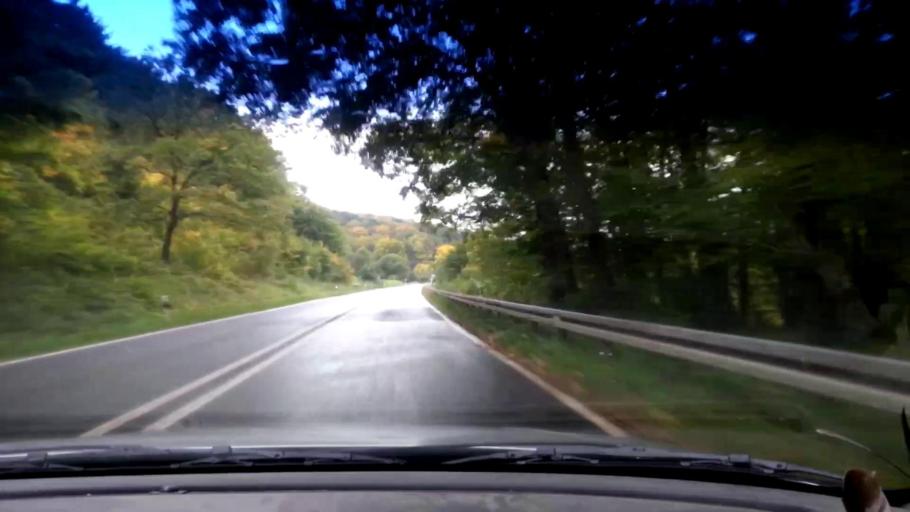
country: DE
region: Bavaria
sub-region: Upper Franconia
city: Poxdorf
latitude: 49.9773
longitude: 11.0982
